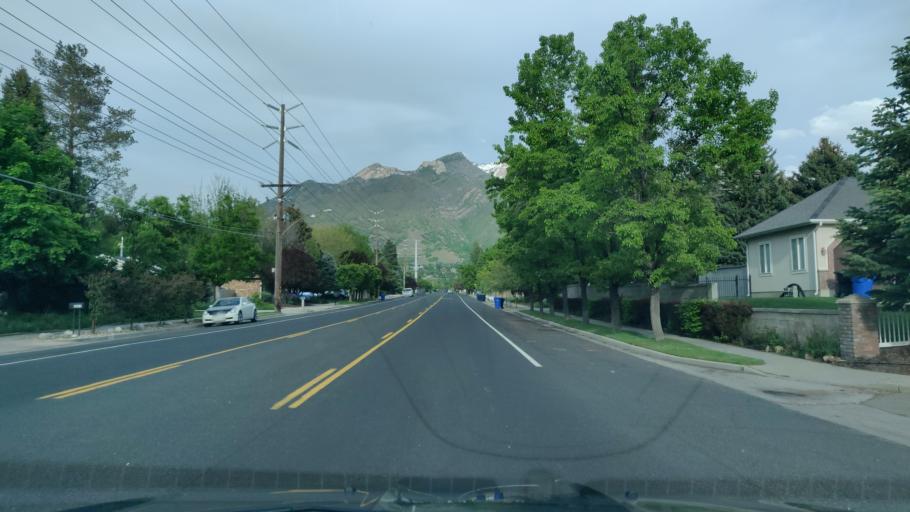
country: US
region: Utah
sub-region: Salt Lake County
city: Little Cottonwood Creek Valley
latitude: 40.6023
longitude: -111.8278
